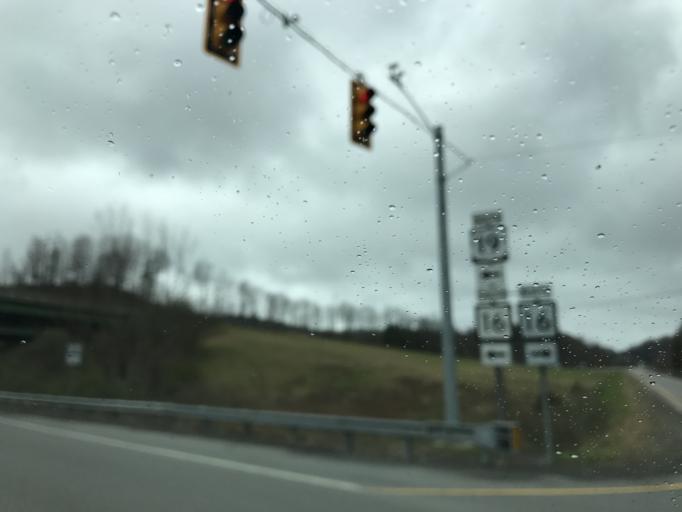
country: US
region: West Virginia
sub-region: Raleigh County
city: Bradley
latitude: 37.8518
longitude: -81.1971
